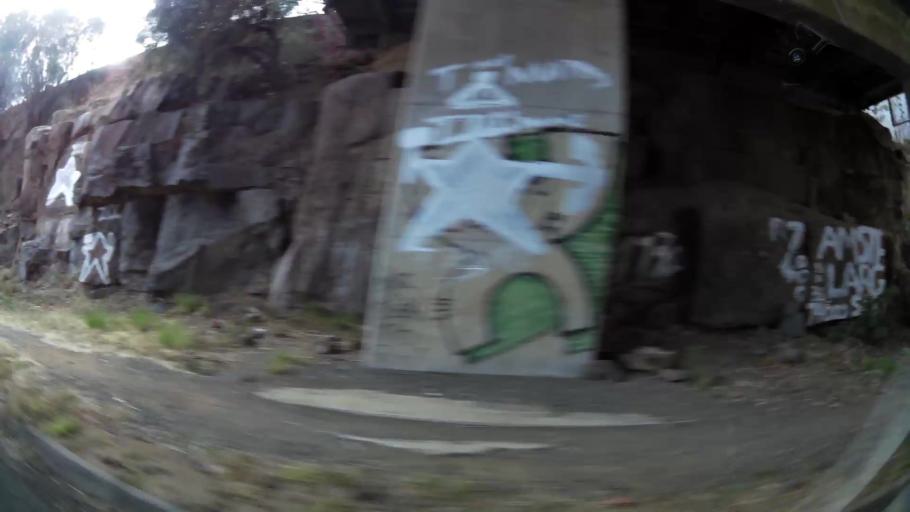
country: ZA
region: Orange Free State
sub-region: Mangaung Metropolitan Municipality
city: Bloemfontein
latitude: -29.1097
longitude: 26.1840
